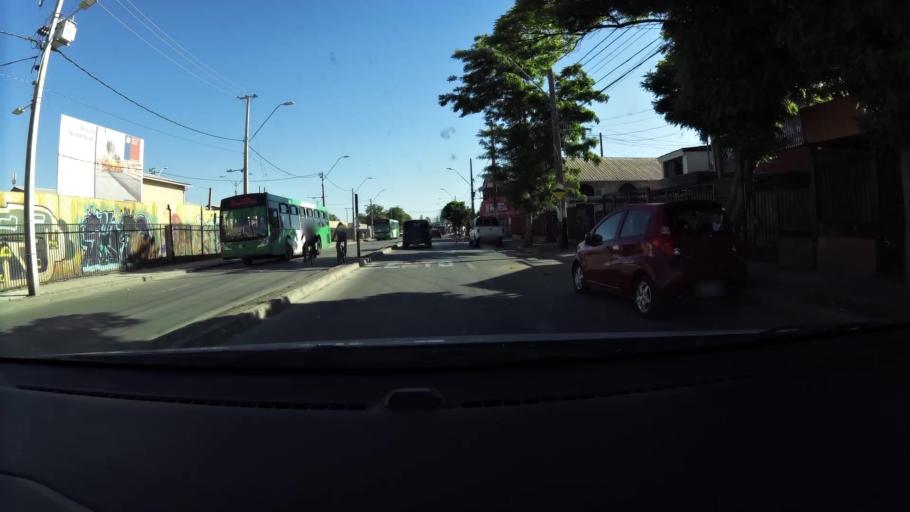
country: CL
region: Santiago Metropolitan
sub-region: Provincia de Maipo
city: San Bernardo
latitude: -33.5988
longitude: -70.6843
